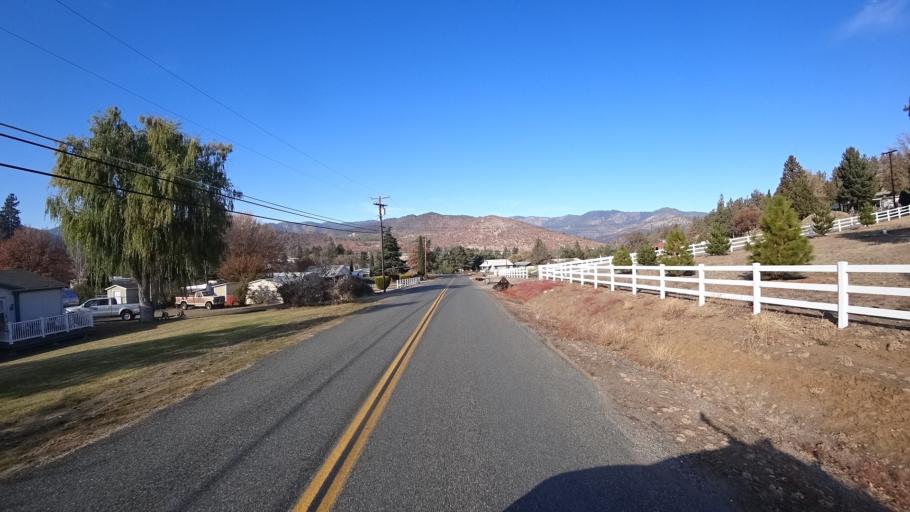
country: US
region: California
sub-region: Siskiyou County
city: Yreka
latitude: 41.6997
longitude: -122.6357
